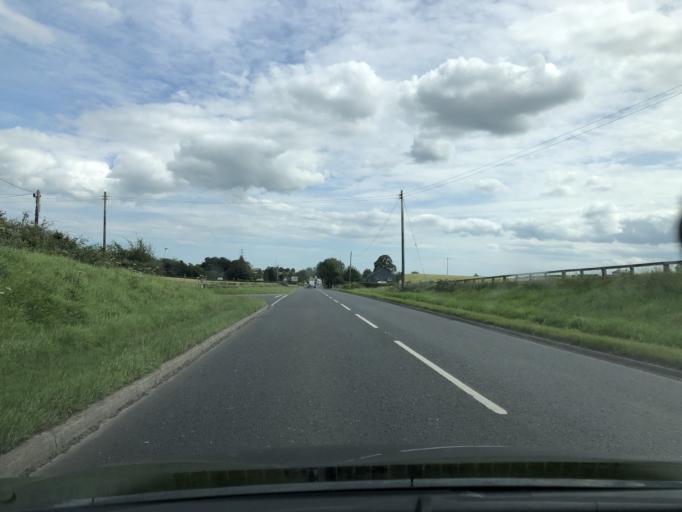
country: GB
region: Northern Ireland
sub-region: Lisburn District
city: Lisburn
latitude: 54.4907
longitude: -5.9997
